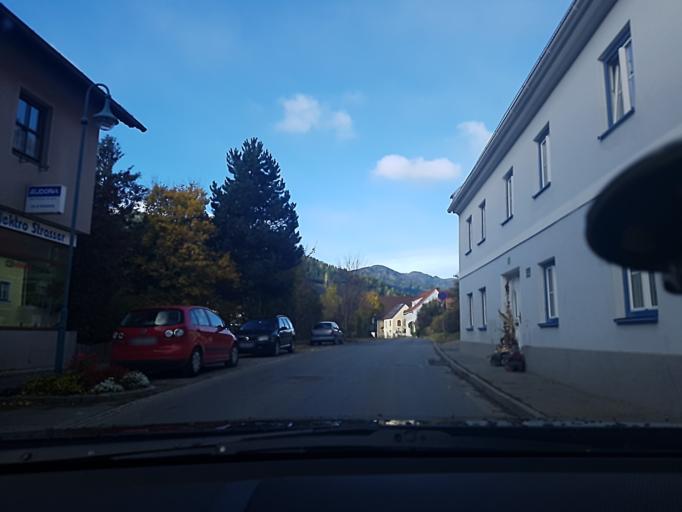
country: AT
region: Styria
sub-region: Politischer Bezirk Murtal
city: Oberzeiring
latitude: 47.2526
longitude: 14.4900
